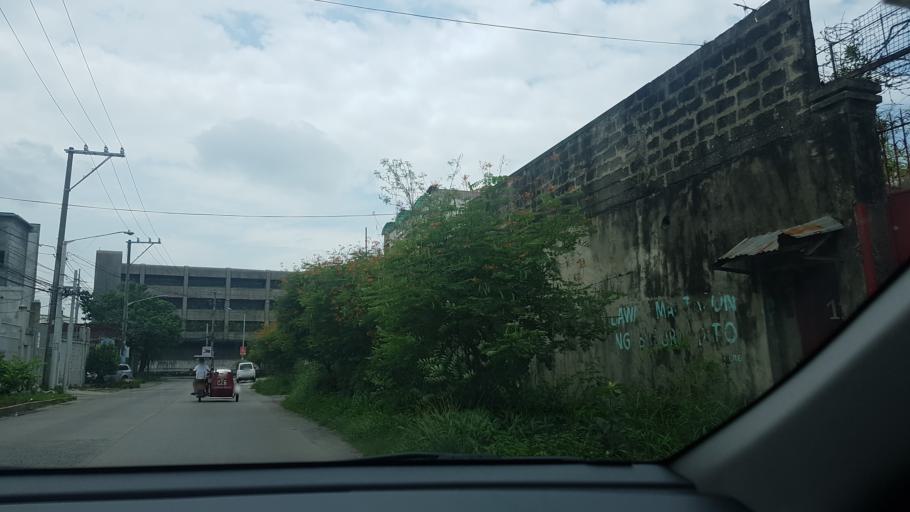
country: PH
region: Calabarzon
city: Del Monte
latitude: 14.6470
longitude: 121.0053
